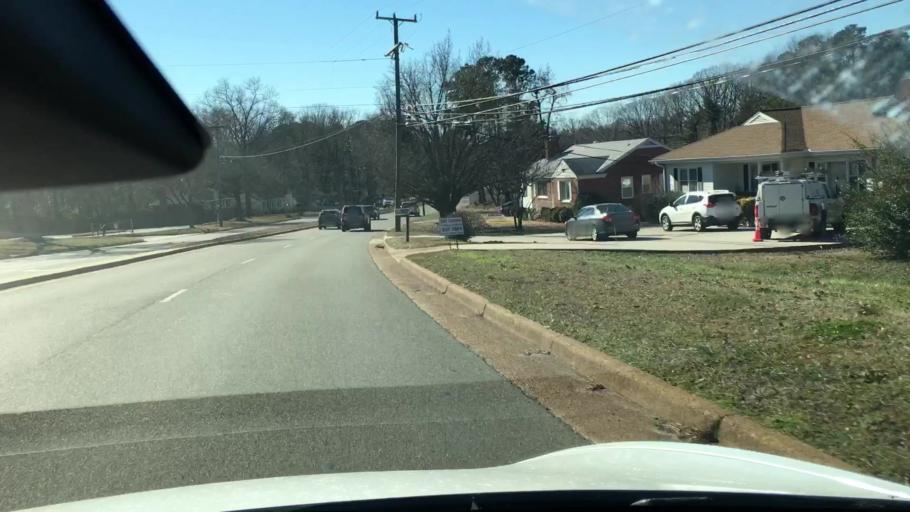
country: US
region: Virginia
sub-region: Henrico County
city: Tuckahoe
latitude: 37.5917
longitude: -77.5682
